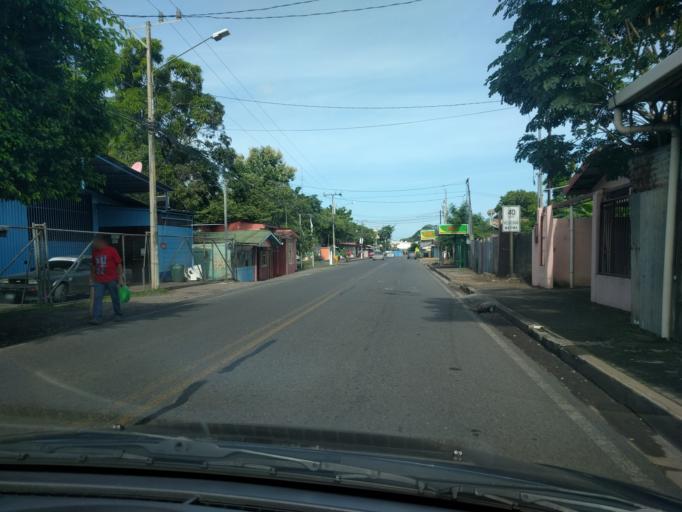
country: CR
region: Puntarenas
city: Esparza
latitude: 9.9902
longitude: -84.7089
